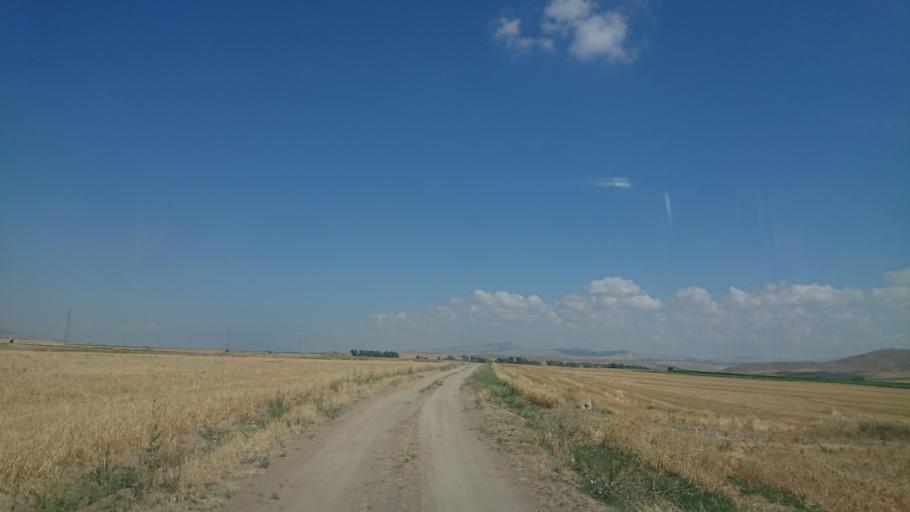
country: TR
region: Aksaray
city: Sariyahsi
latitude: 38.9867
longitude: 33.9031
